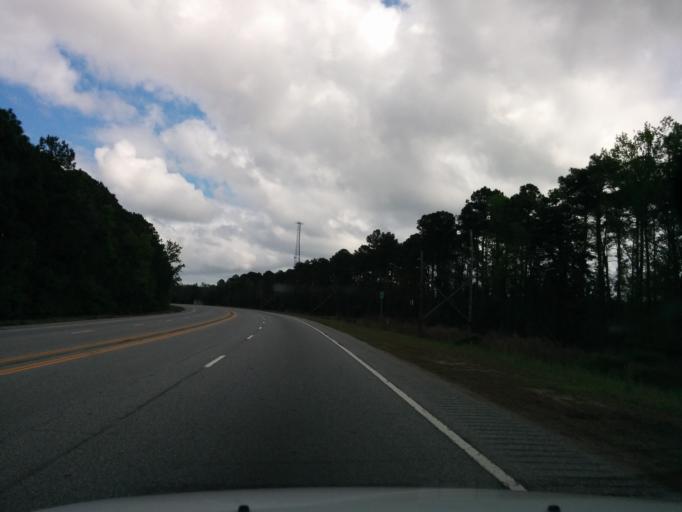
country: US
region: Georgia
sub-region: Glynn County
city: Brunswick
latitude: 31.1156
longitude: -81.5374
